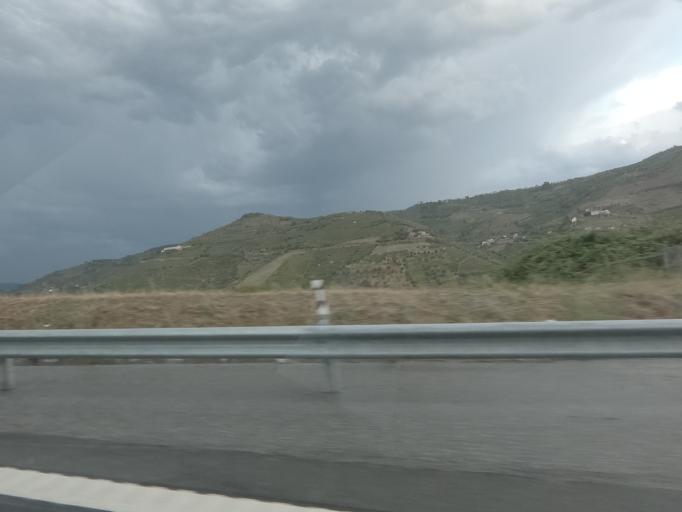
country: PT
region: Vila Real
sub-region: Peso da Regua
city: Peso da Regua
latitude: 41.1788
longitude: -7.7504
